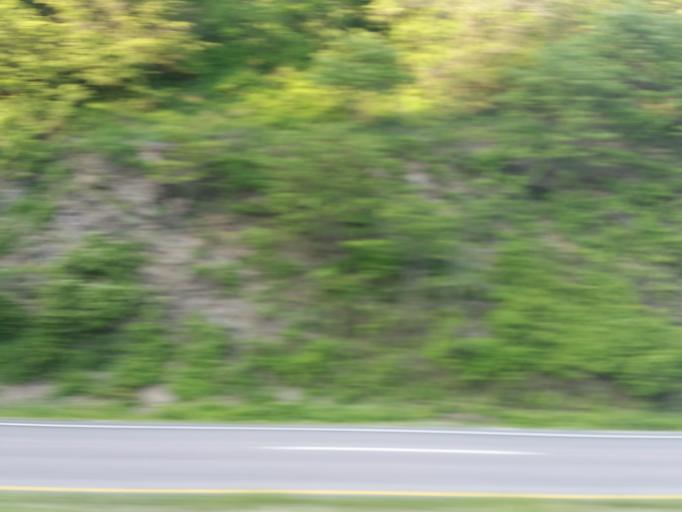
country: US
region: Virginia
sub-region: Washington County
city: Abingdon
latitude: 36.7432
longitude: -82.0477
